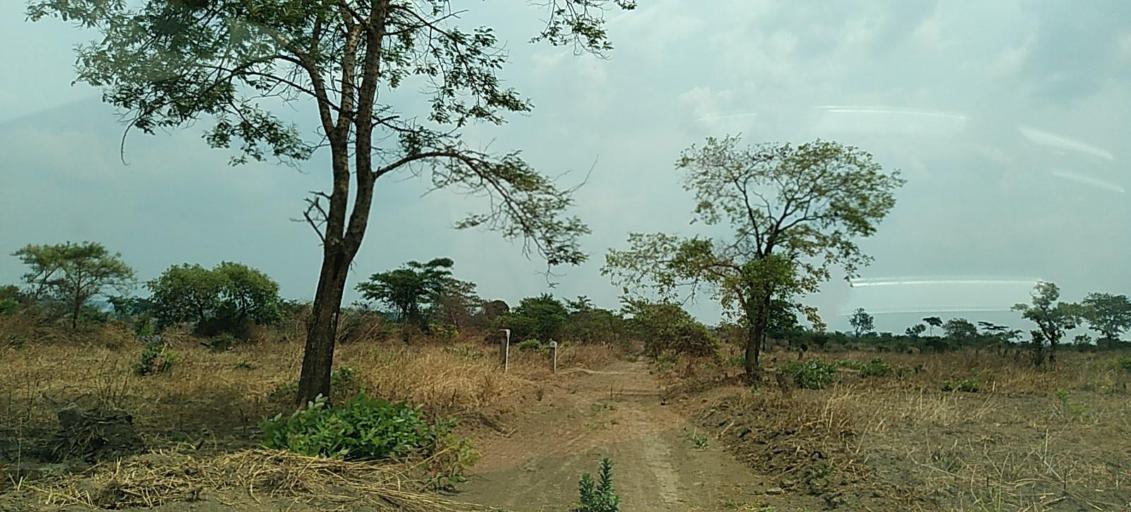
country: ZM
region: Copperbelt
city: Chililabombwe
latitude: -12.3604
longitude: 27.8007
